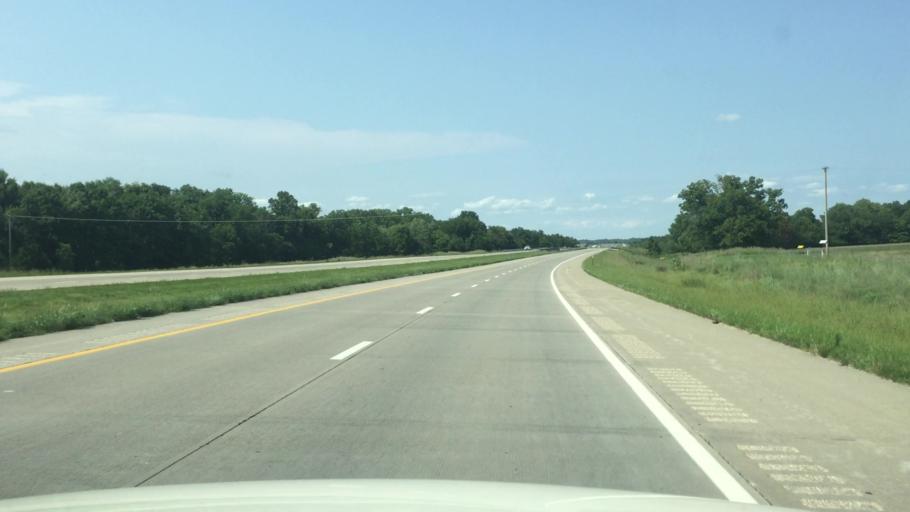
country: US
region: Kansas
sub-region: Linn County
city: La Cygne
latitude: 38.2961
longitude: -94.6772
